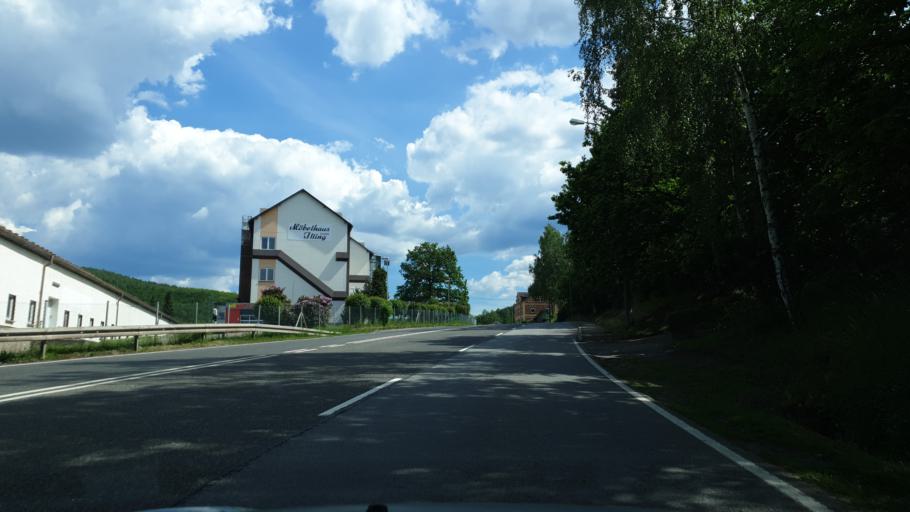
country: DE
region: Saxony
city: Aue
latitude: 50.5781
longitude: 12.7157
